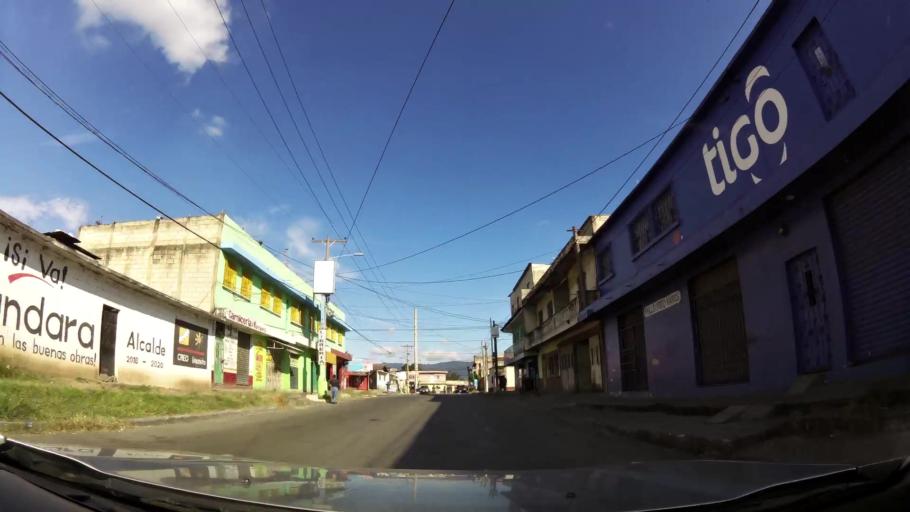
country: GT
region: Guatemala
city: Villa Nueva
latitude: 14.5217
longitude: -90.5756
